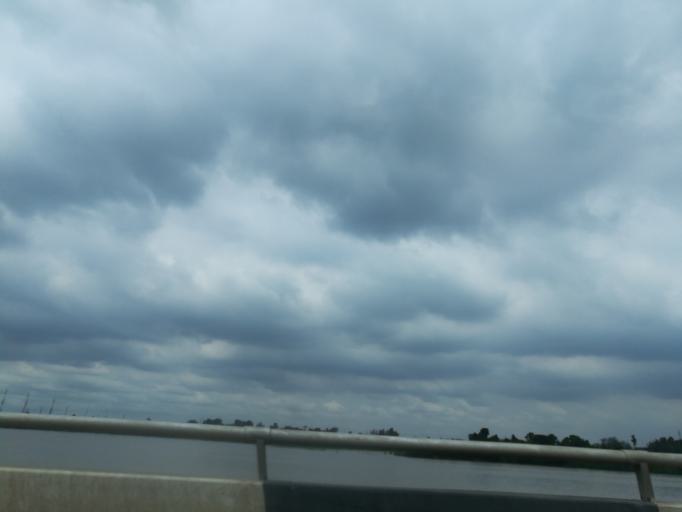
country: NG
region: Lagos
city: Makoko
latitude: 6.5104
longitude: 3.4048
